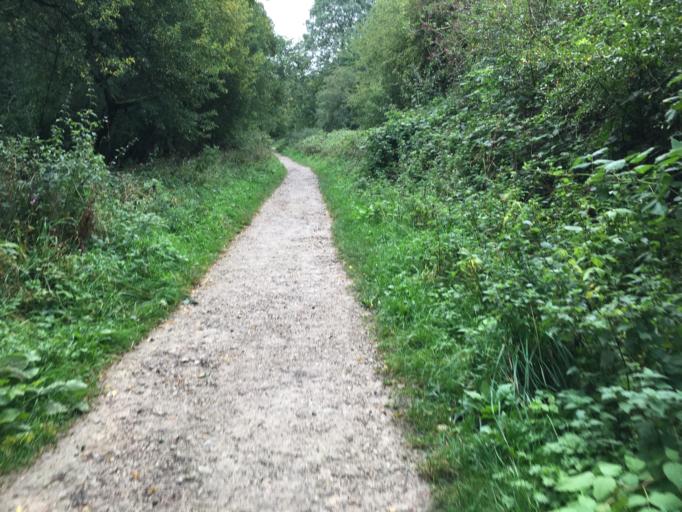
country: GB
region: England
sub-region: North Yorkshire
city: Sleights
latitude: 54.4067
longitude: -0.7335
